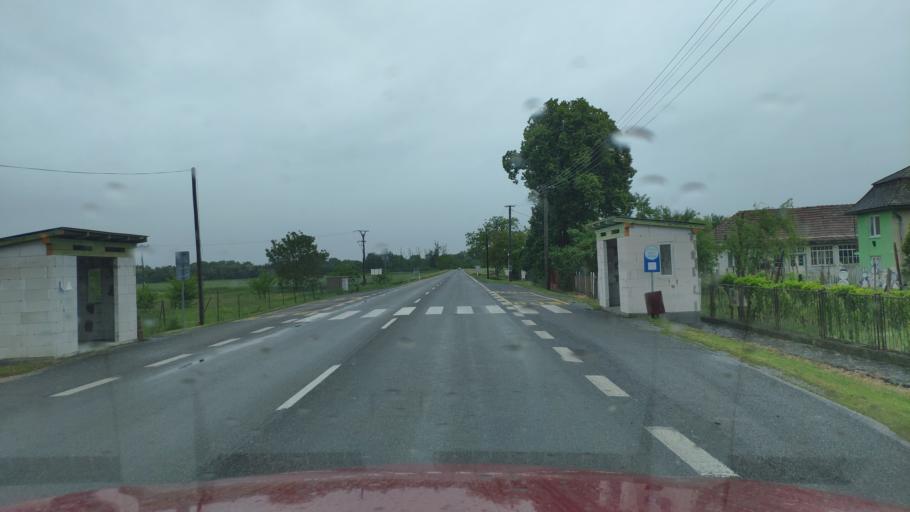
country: HU
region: Borsod-Abauj-Zemplen
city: Karcsa
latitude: 48.4286
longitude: 21.8471
